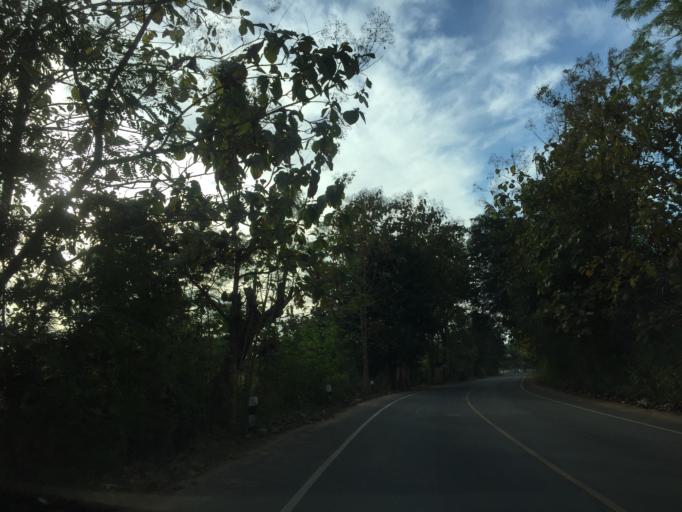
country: TH
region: Lamphun
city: Lamphun
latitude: 18.5106
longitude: 99.0289
